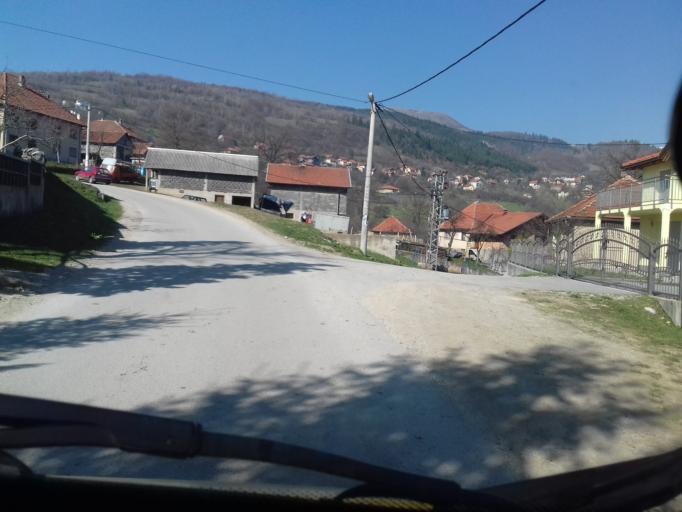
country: BA
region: Federation of Bosnia and Herzegovina
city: Travnik
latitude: 44.2560
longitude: 17.7359
